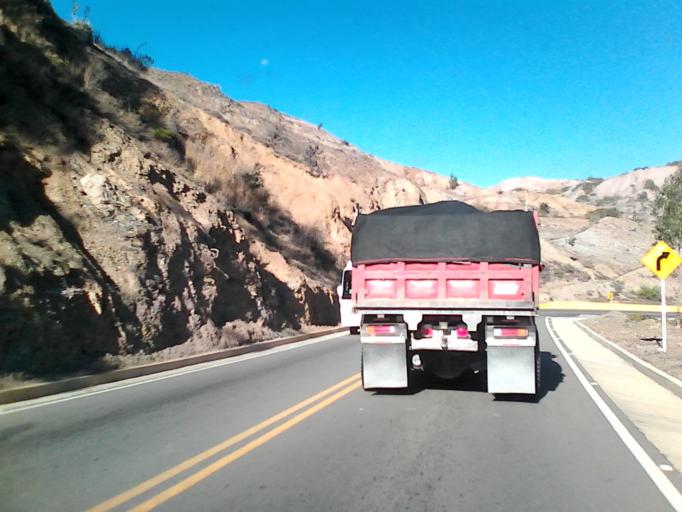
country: CO
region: Boyaca
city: Sachica
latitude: 5.5771
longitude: -73.5129
